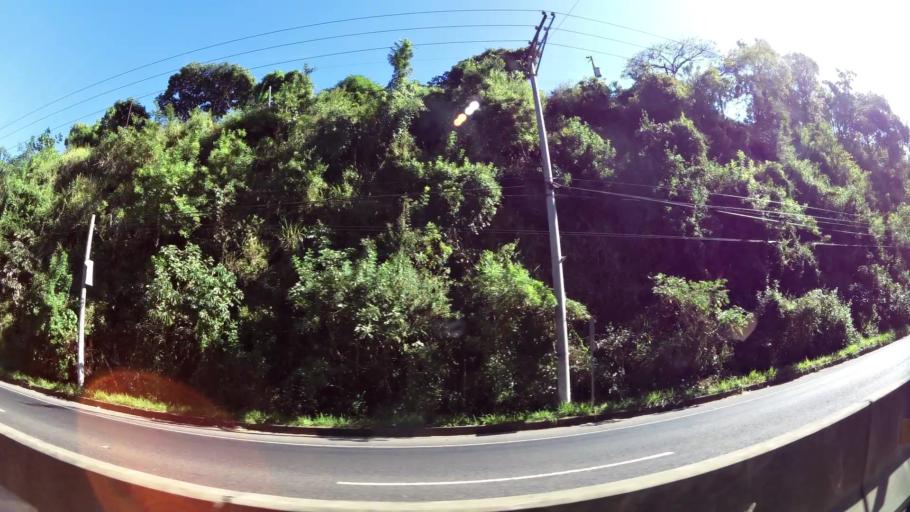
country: SV
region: Santa Ana
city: Santa Ana
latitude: 13.9462
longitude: -89.5565
